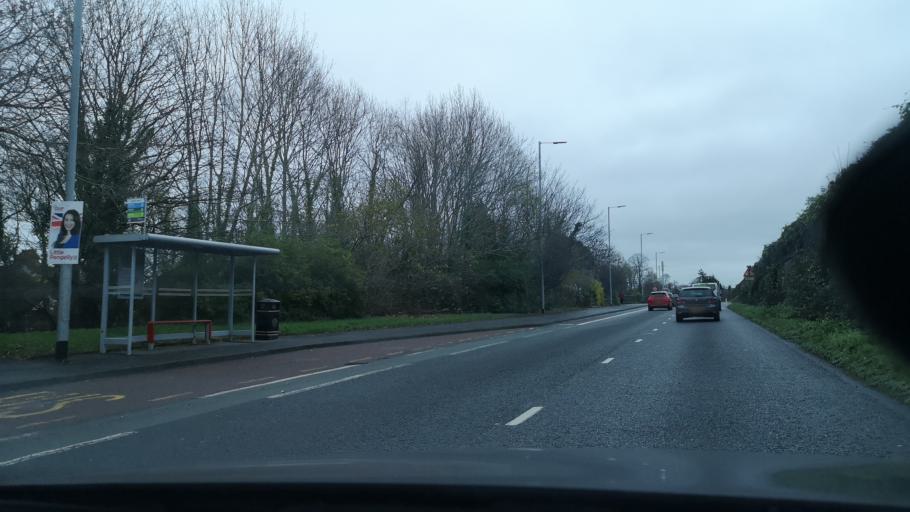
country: GB
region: Northern Ireland
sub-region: Castlereagh District
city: Castlereagh
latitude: 54.5682
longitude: -5.8979
